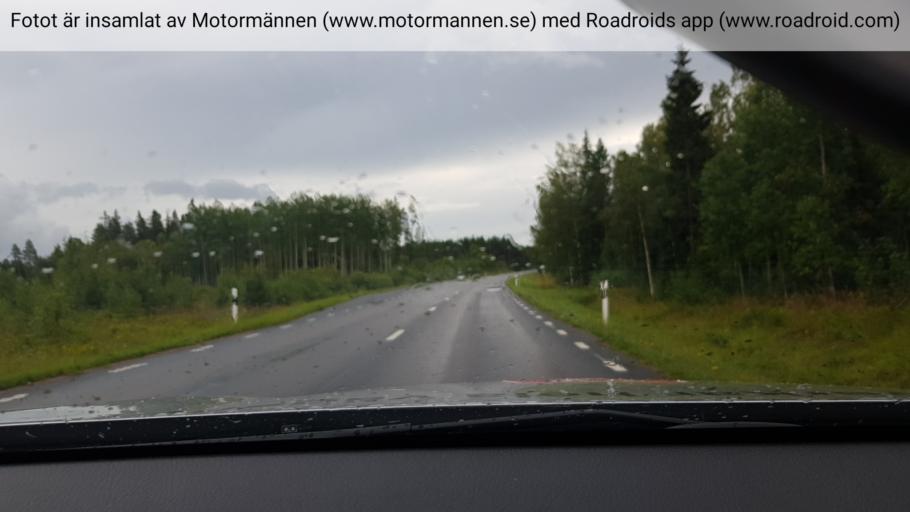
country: SE
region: Uppsala
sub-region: Tierps Kommun
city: Karlholmsbruk
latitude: 60.5327
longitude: 17.5839
